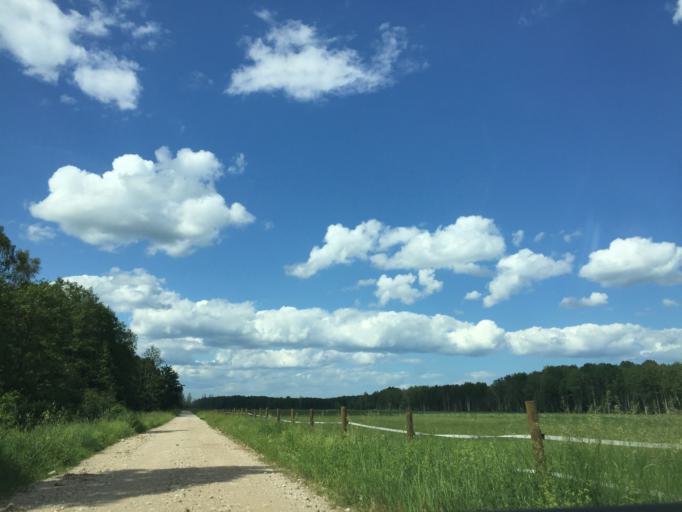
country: LV
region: Engure
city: Smarde
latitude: 56.8536
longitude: 23.3960
